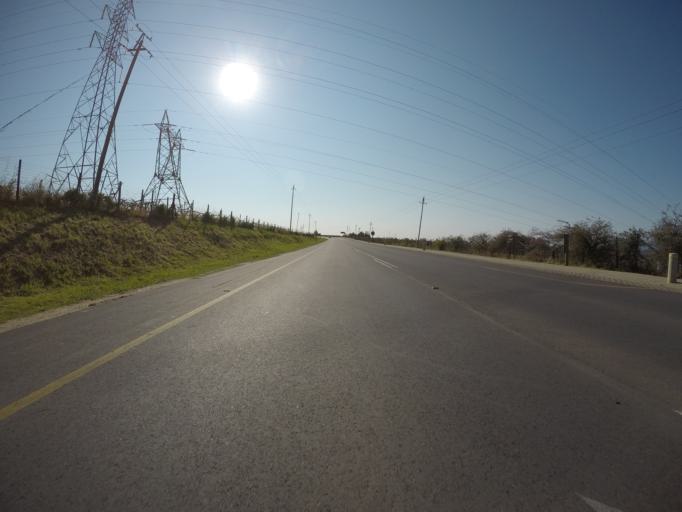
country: ZA
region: Western Cape
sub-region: Cape Winelands District Municipality
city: Noorder-Paarl
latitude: -33.6742
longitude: 18.9331
